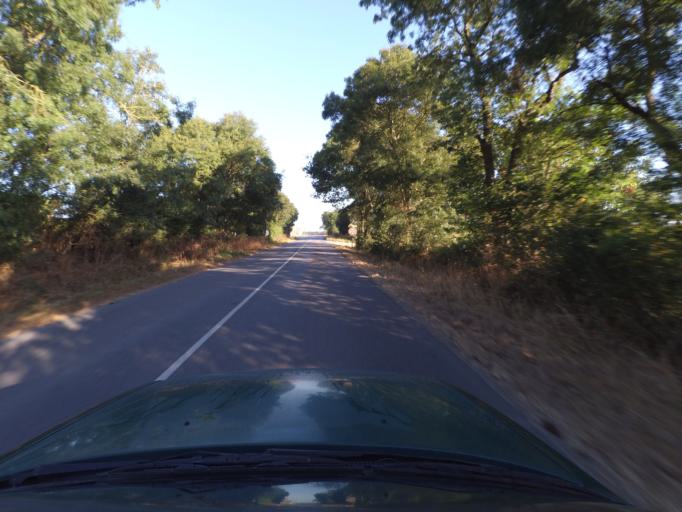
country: FR
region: Pays de la Loire
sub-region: Departement de la Loire-Atlantique
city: La Planche
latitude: 46.9954
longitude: -1.4529
